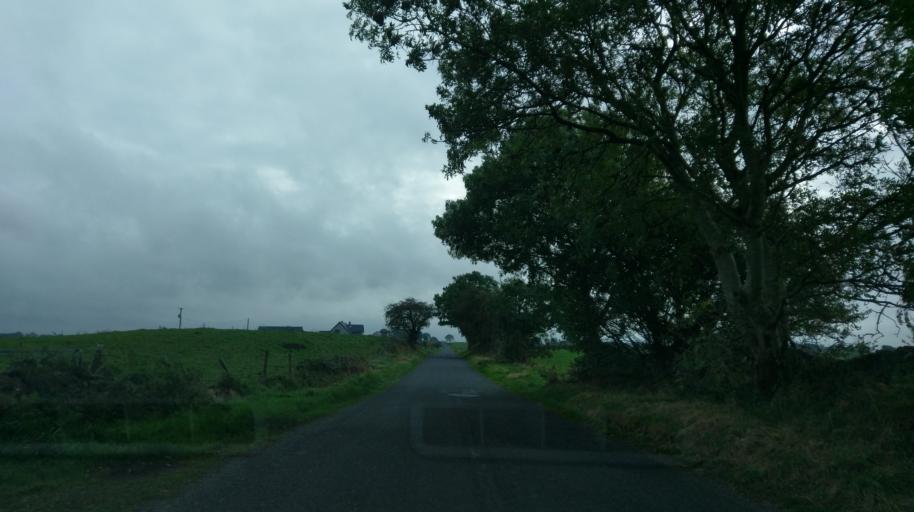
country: IE
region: Connaught
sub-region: County Galway
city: Athenry
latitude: 53.4612
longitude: -8.6240
